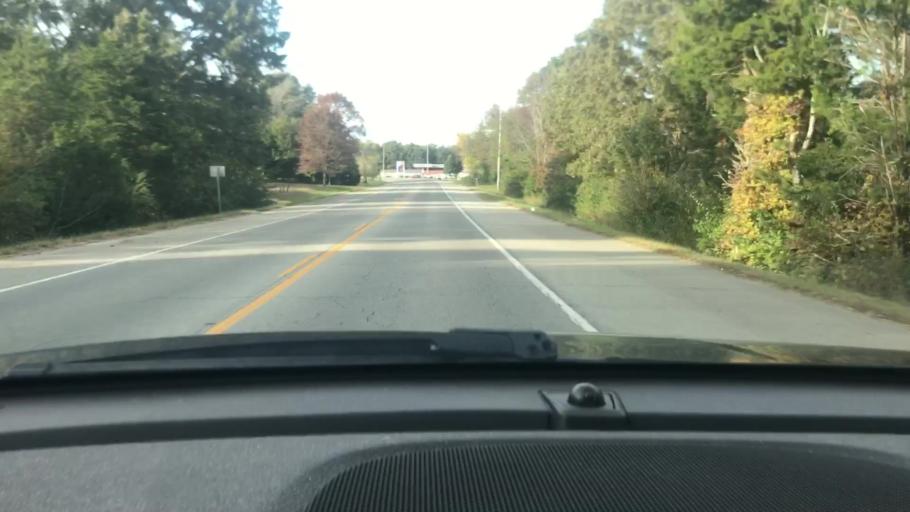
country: US
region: Tennessee
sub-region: Dickson County
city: White Bluff
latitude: 36.1232
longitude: -87.2270
